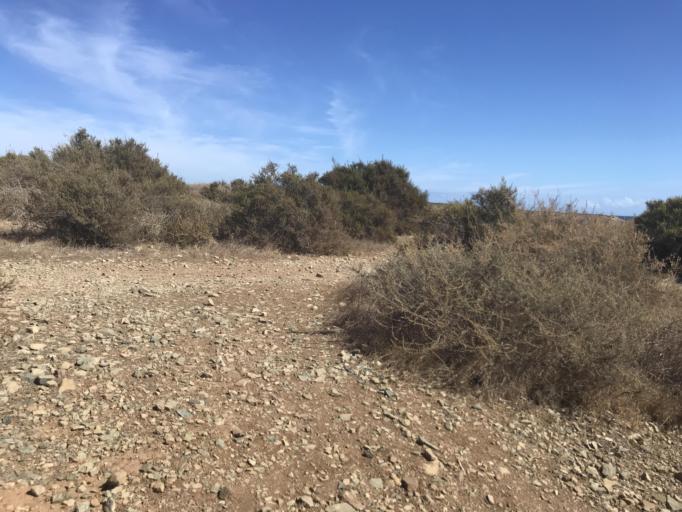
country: ES
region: Valencia
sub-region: Provincia de Alicante
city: Santa Pola
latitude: 38.1634
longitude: -0.4759
